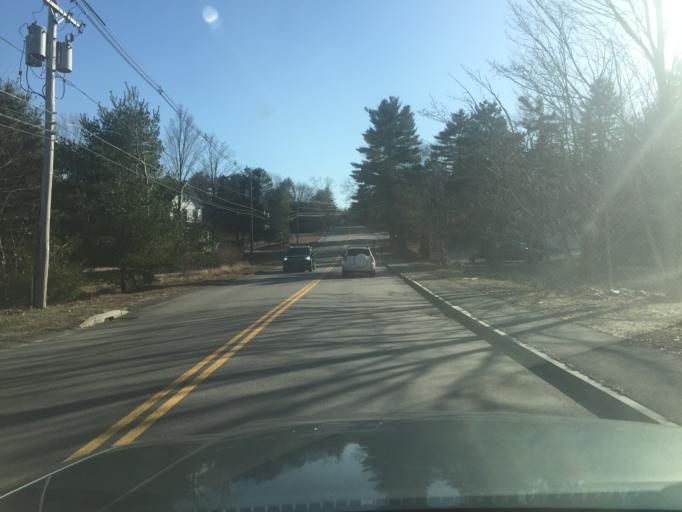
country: US
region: Massachusetts
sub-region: Norfolk County
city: Franklin
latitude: 42.1008
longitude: -71.3717
